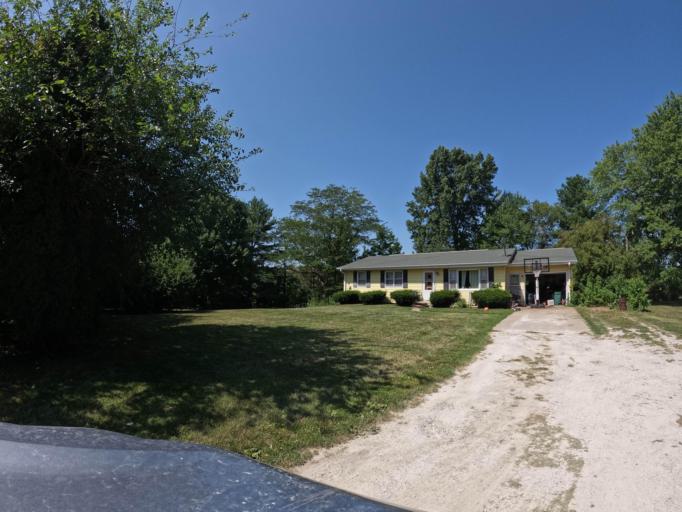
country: US
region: Iowa
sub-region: Henry County
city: Mount Pleasant
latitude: 40.9329
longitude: -91.5382
